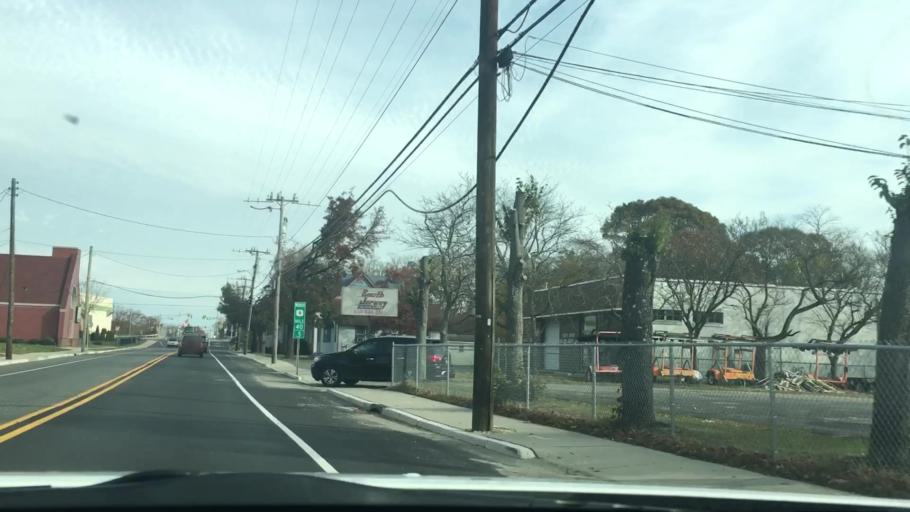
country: US
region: New Jersey
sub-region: Atlantic County
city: Pleasantville
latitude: 39.3997
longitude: -74.5256
